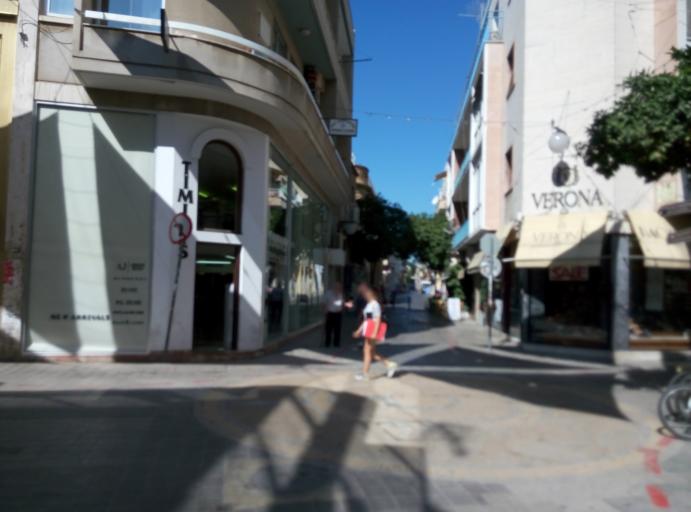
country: CY
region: Lefkosia
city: Nicosia
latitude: 35.1717
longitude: 33.3614
